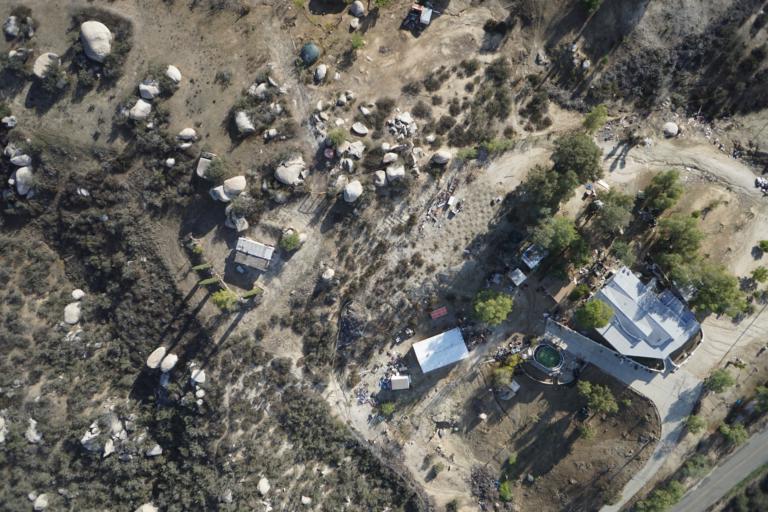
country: US
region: California
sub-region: Riverside County
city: East Hemet
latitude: 33.6417
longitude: -116.9229
